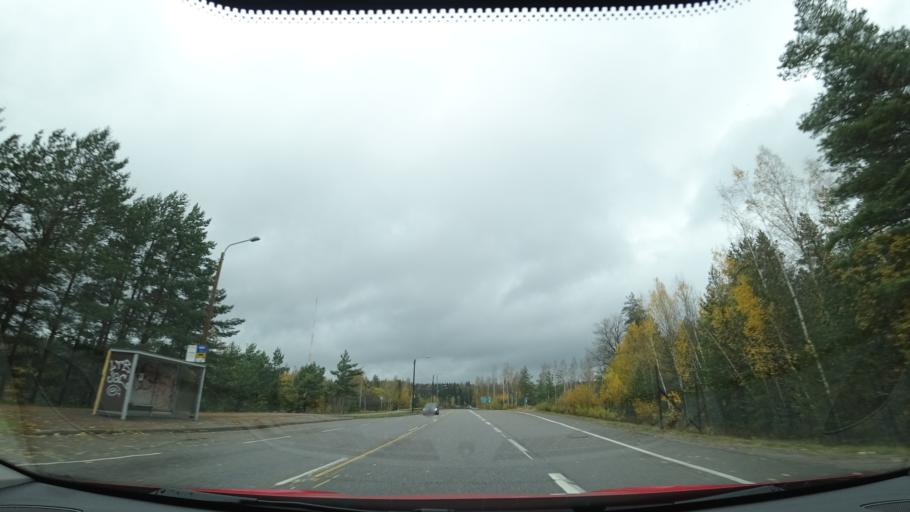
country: FI
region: Uusimaa
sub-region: Helsinki
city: Sibbo
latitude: 60.2650
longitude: 25.2103
